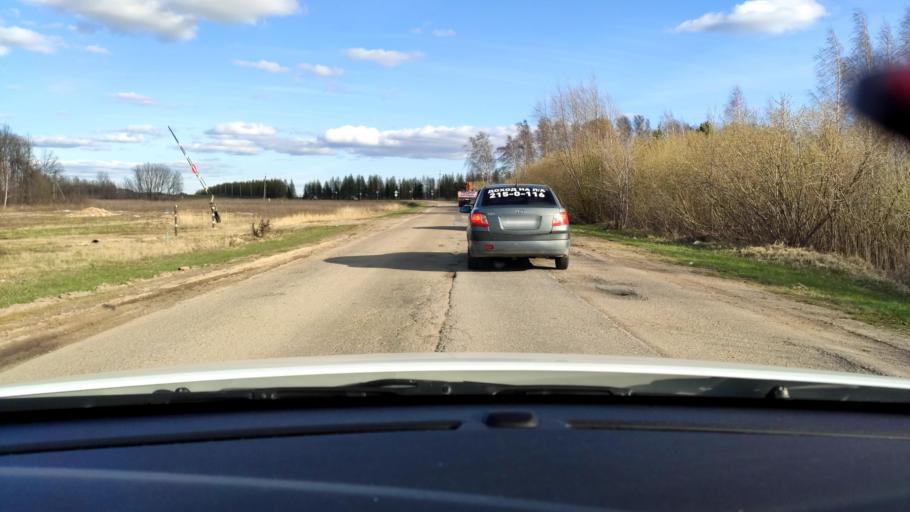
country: RU
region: Tatarstan
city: Vysokaya Gora
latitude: 55.8950
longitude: 49.3329
